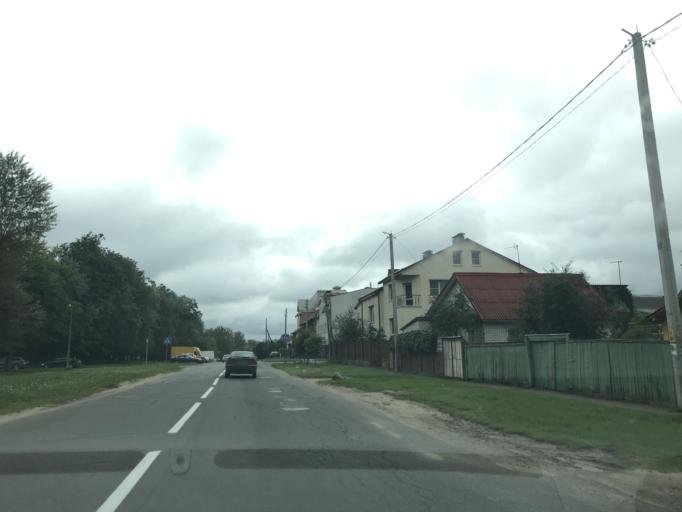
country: BY
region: Minsk
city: Minsk
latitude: 53.9409
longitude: 27.6131
